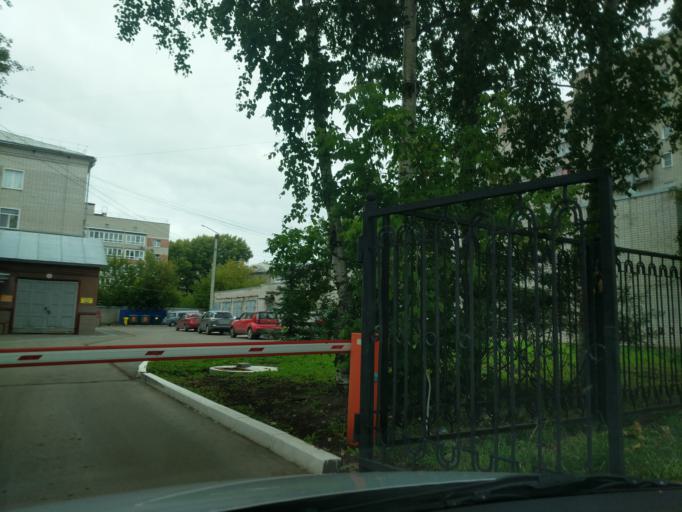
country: RU
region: Kirov
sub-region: Kirovo-Chepetskiy Rayon
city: Kirov
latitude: 58.6380
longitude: 49.6199
